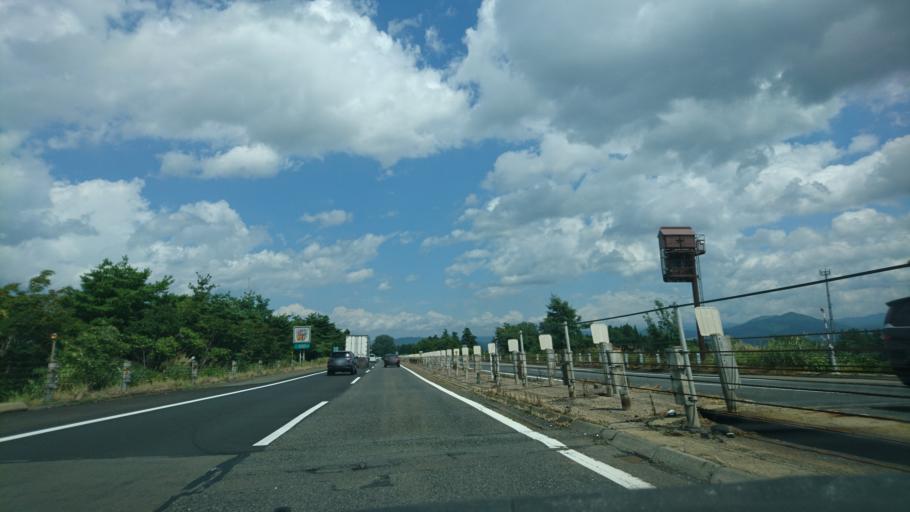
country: JP
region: Iwate
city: Morioka-shi
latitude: 39.6045
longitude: 141.1236
